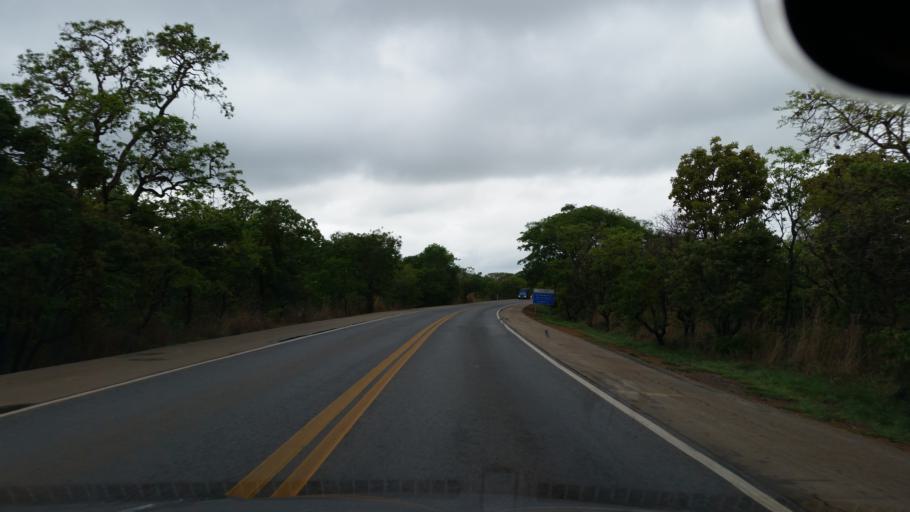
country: BR
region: Goias
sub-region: Luziania
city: Luziania
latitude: -16.4485
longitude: -47.8088
